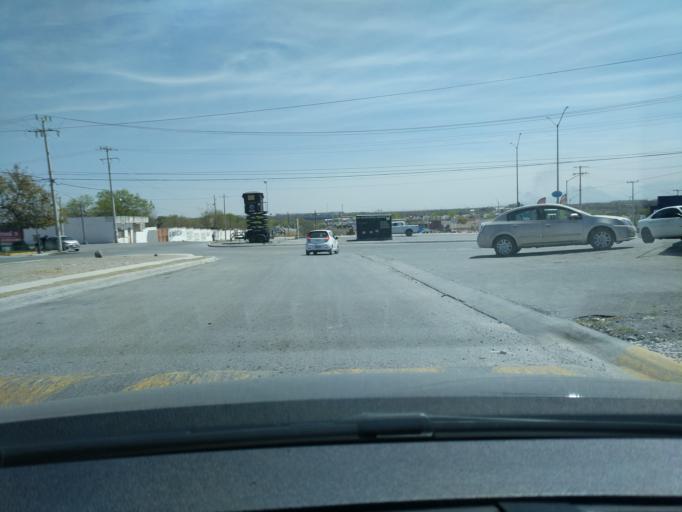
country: MX
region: Nuevo Leon
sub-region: Salinas Victoria
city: Las Torres
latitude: 25.9607
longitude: -100.3020
